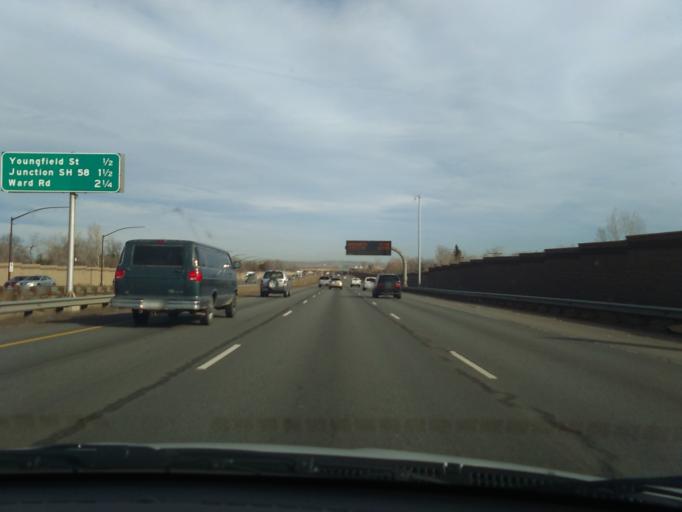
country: US
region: Colorado
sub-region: Jefferson County
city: Applewood
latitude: 39.7491
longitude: -105.1494
